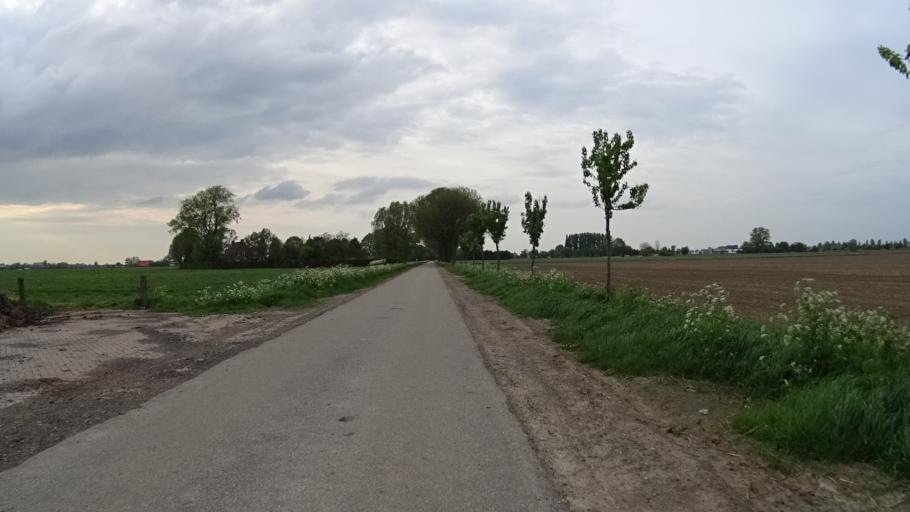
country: NL
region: North Brabant
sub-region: Gemeente Aalburg
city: Aalburg
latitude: 51.7545
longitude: 5.1007
